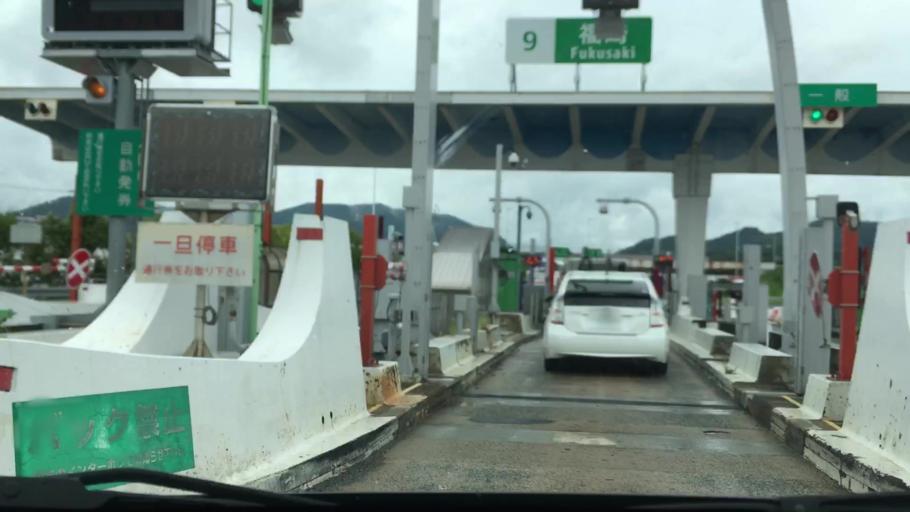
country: JP
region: Hyogo
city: Himeji
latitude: 34.9470
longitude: 134.7616
